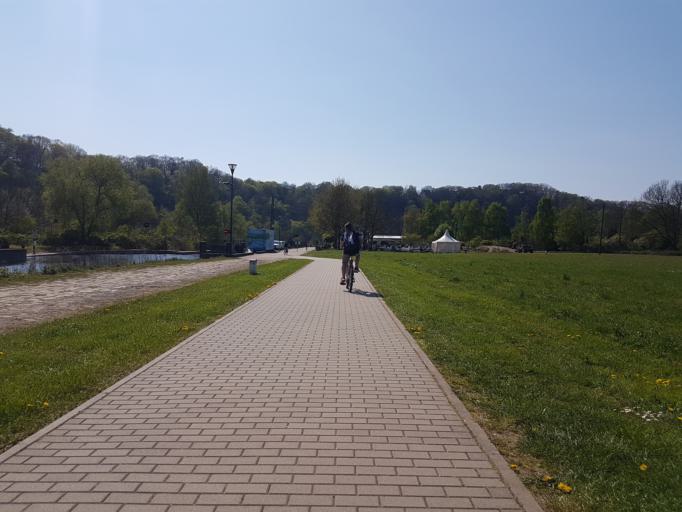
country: DE
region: North Rhine-Westphalia
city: Witten
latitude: 51.4224
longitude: 7.3008
